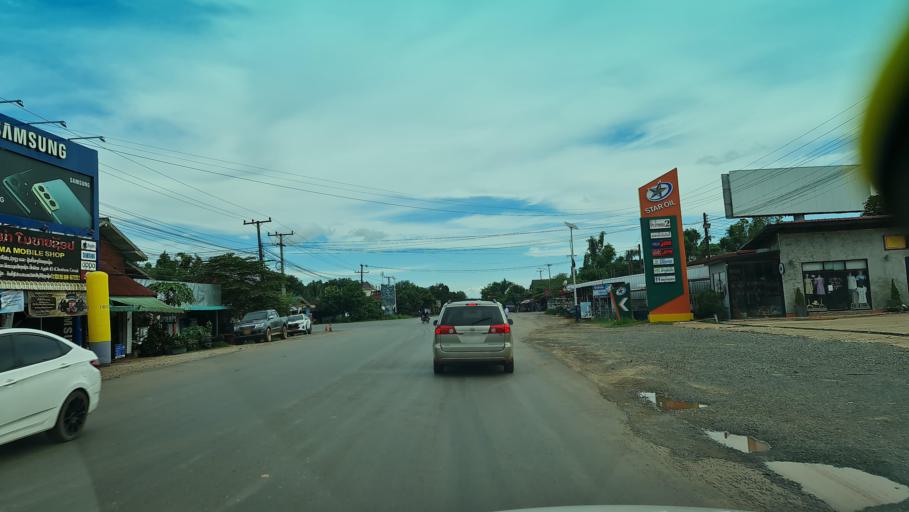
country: TH
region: Nakhon Phanom
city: Ban Phaeng
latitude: 18.0986
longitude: 104.2867
